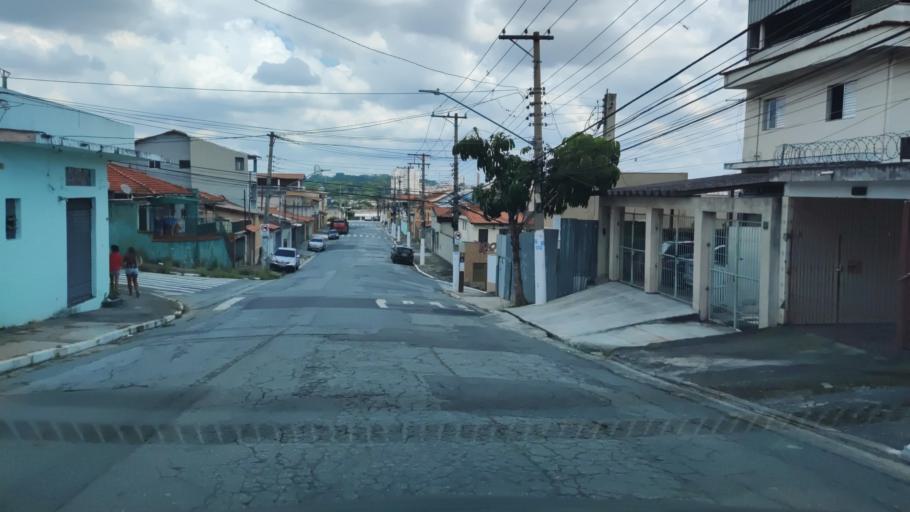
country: BR
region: Sao Paulo
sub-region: Sao Caetano Do Sul
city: Sao Caetano do Sul
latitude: -23.5480
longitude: -46.5181
